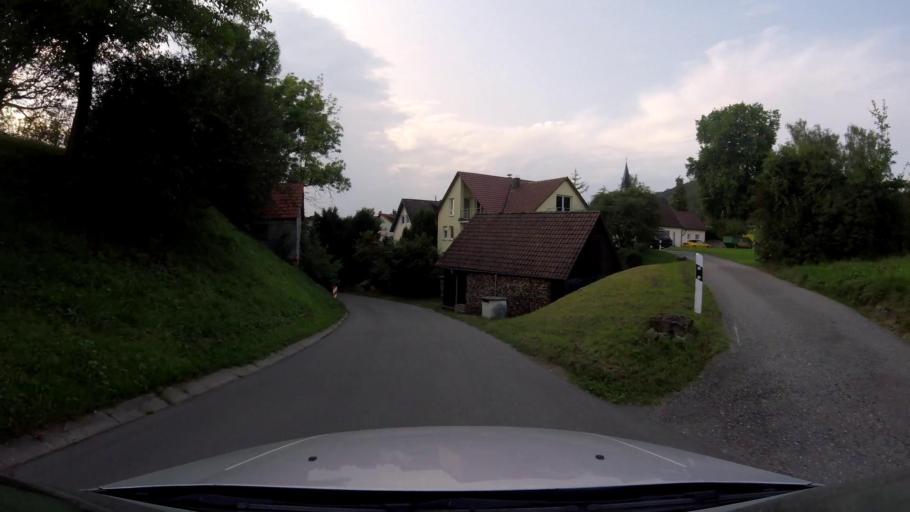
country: DE
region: Baden-Wuerttemberg
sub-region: Regierungsbezirk Stuttgart
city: Rudersberg
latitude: 48.8588
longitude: 9.5536
